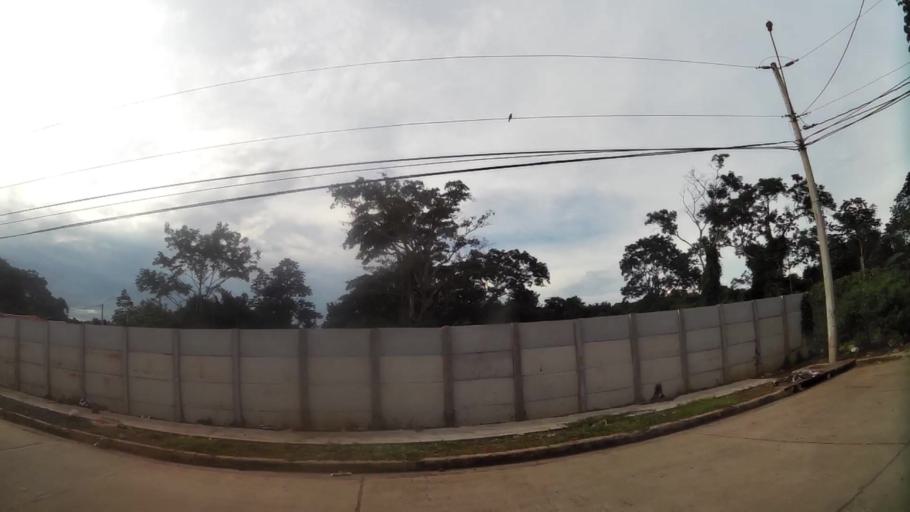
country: PA
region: Panama
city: La Chorrera
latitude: 8.8873
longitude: -79.7567
